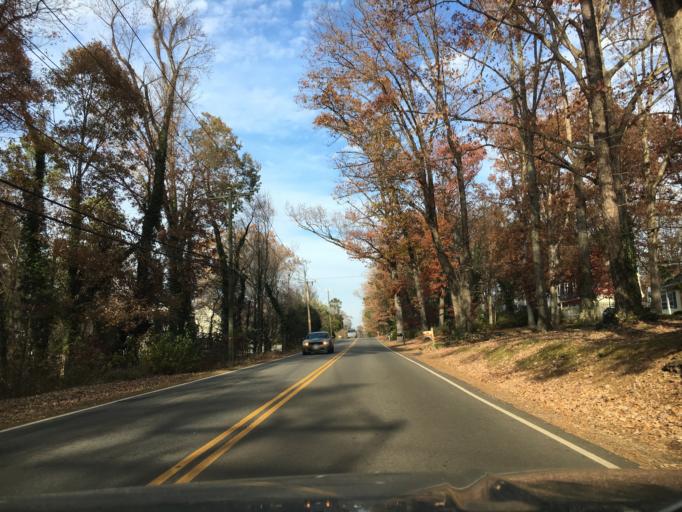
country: US
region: Virginia
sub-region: Henrico County
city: Tuckahoe
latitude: 37.5950
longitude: -77.5483
